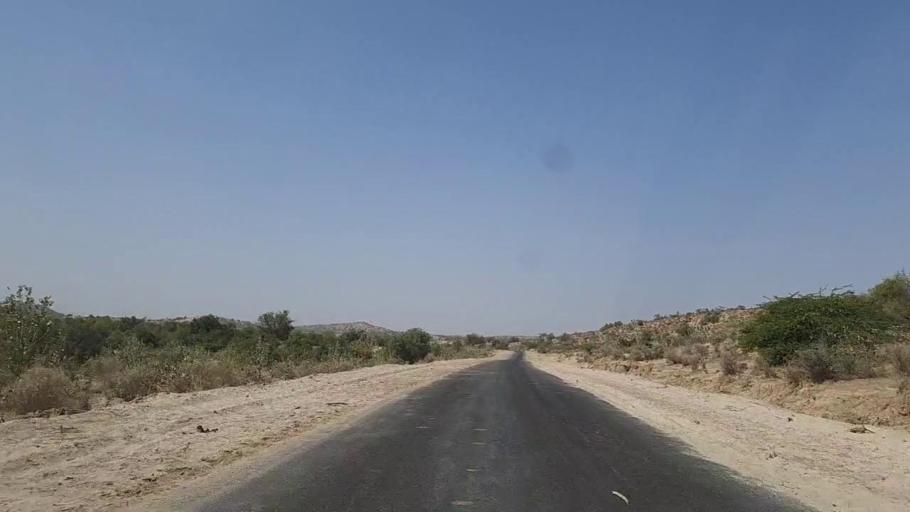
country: PK
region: Sindh
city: Diplo
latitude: 24.5788
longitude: 69.4982
